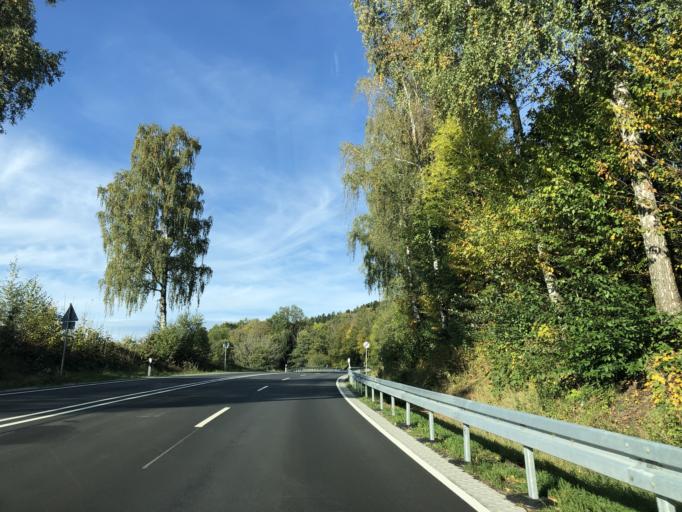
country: DE
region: Bavaria
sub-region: Lower Bavaria
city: Grafling
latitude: 48.8971
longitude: 12.9790
